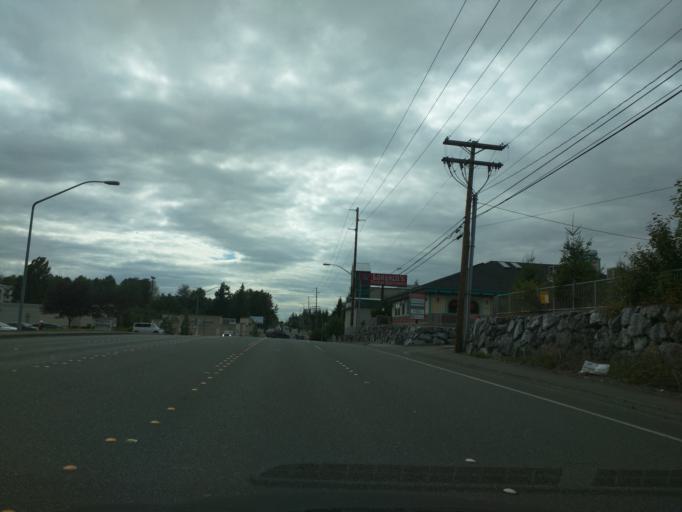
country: US
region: Washington
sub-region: Whatcom County
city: Bellingham
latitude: 48.7898
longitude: -122.4834
